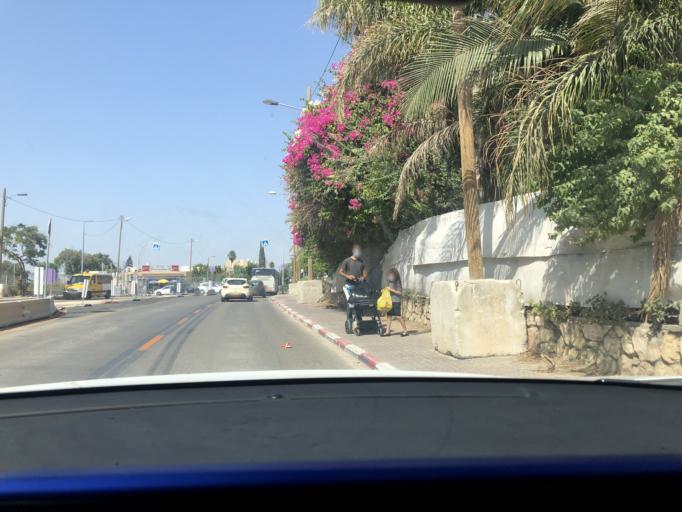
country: IL
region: Central District
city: Lod
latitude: 31.9472
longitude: 34.8802
